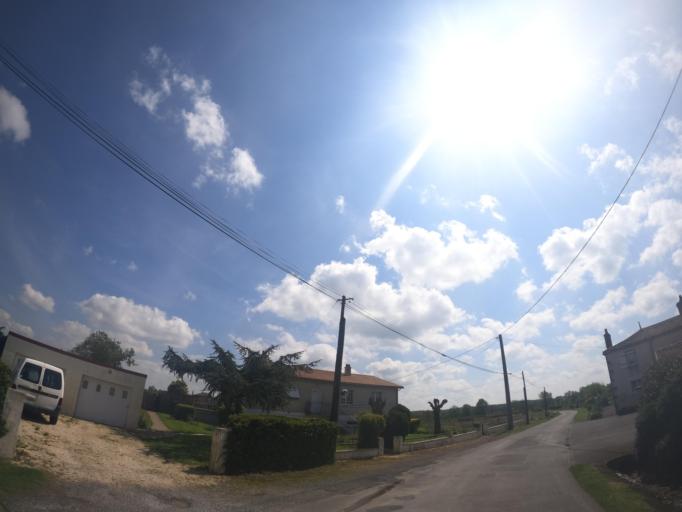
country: FR
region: Poitou-Charentes
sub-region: Departement des Deux-Sevres
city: Saint-Varent
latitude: 46.8573
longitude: -0.2417
